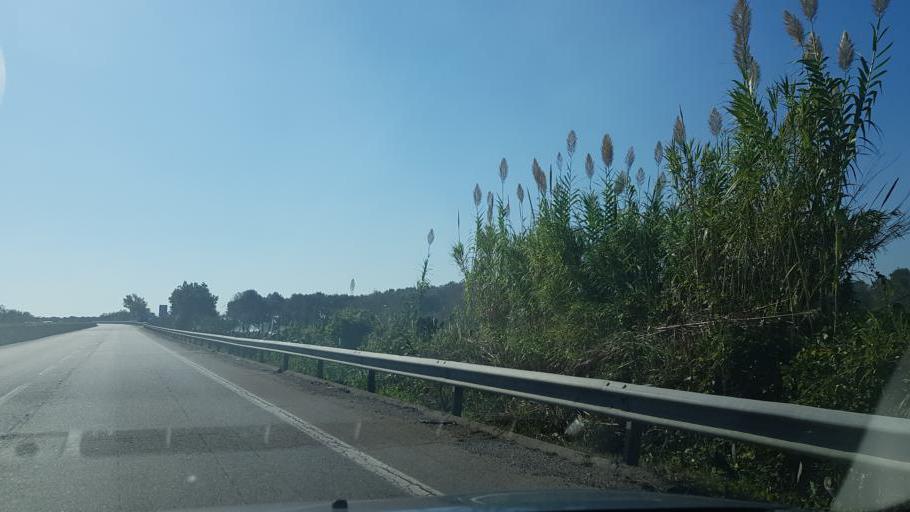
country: IT
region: Apulia
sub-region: Provincia di Brindisi
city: Tuturano
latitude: 40.5444
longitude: 18.0003
